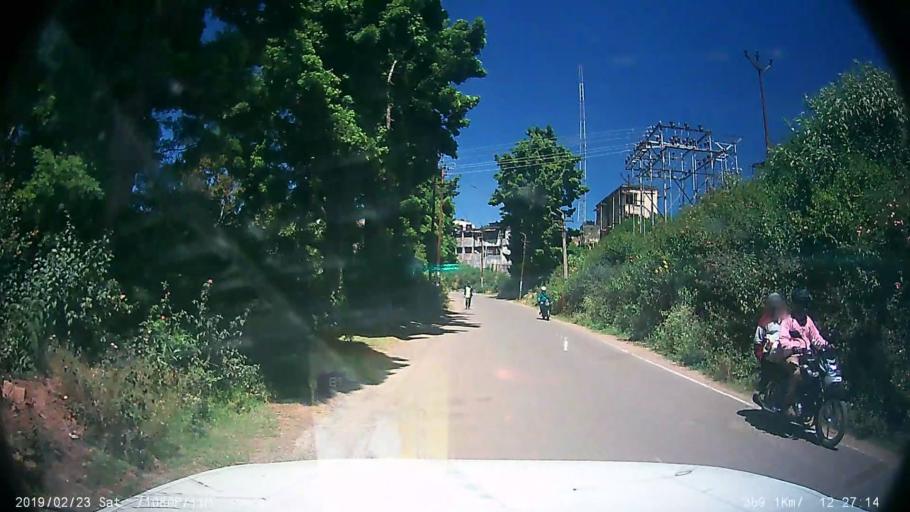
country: IN
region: Tamil Nadu
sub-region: Nilgiri
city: Wellington
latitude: 11.3463
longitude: 76.7863
